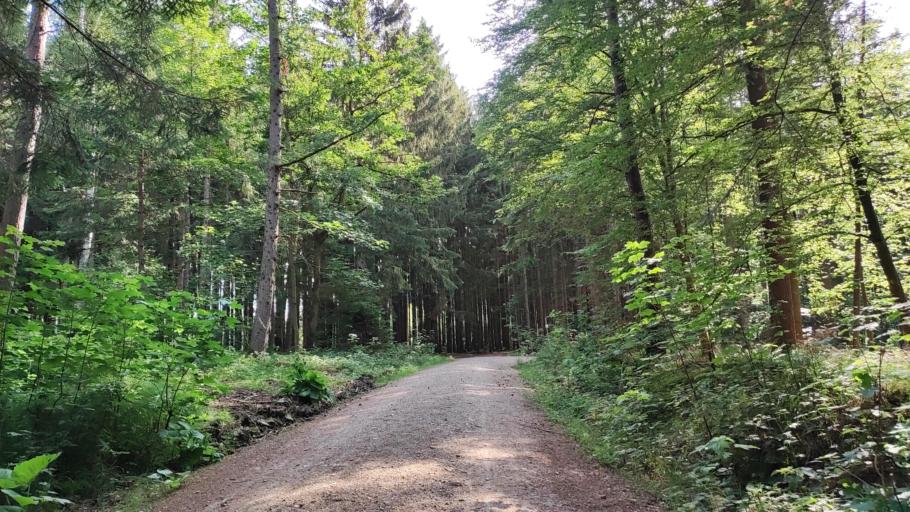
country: DE
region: Bavaria
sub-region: Swabia
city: Altenmunster
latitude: 48.4766
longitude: 10.5711
